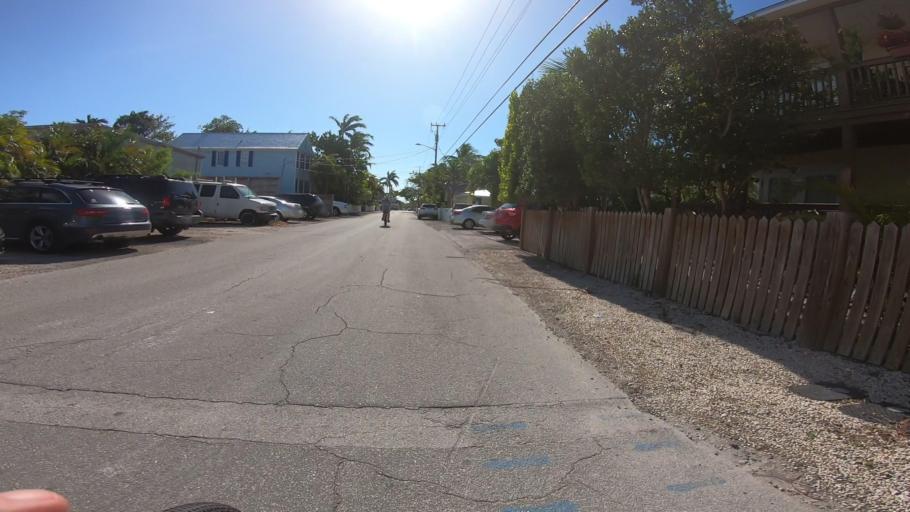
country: US
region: Florida
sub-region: Monroe County
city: Key West
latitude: 24.5510
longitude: -81.7951
